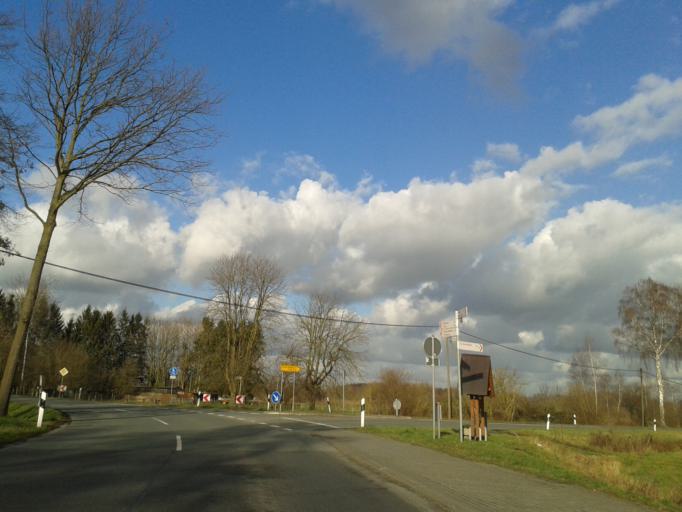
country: DE
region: North Rhine-Westphalia
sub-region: Regierungsbezirk Detmold
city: Salzkotten
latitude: 51.6877
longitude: 8.5705
